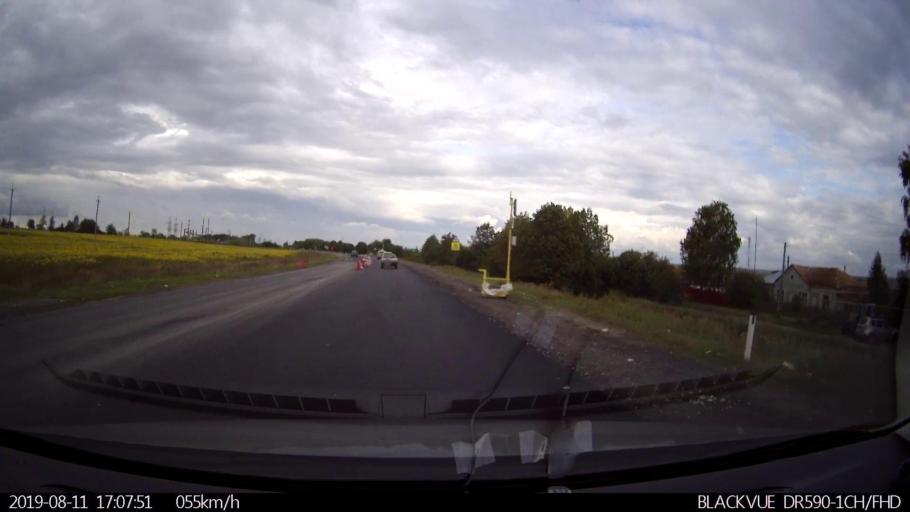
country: RU
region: Ulyanovsk
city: Mayna
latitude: 54.2918
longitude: 47.8307
